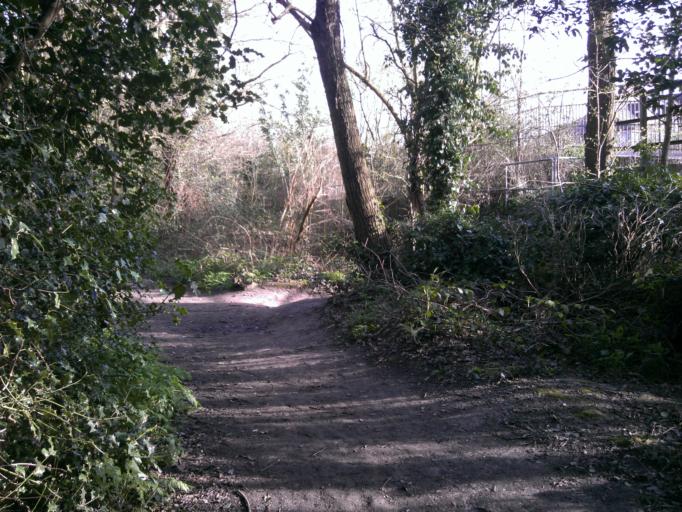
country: GB
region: England
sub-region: Essex
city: Wivenhoe
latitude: 51.8580
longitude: 0.9541
